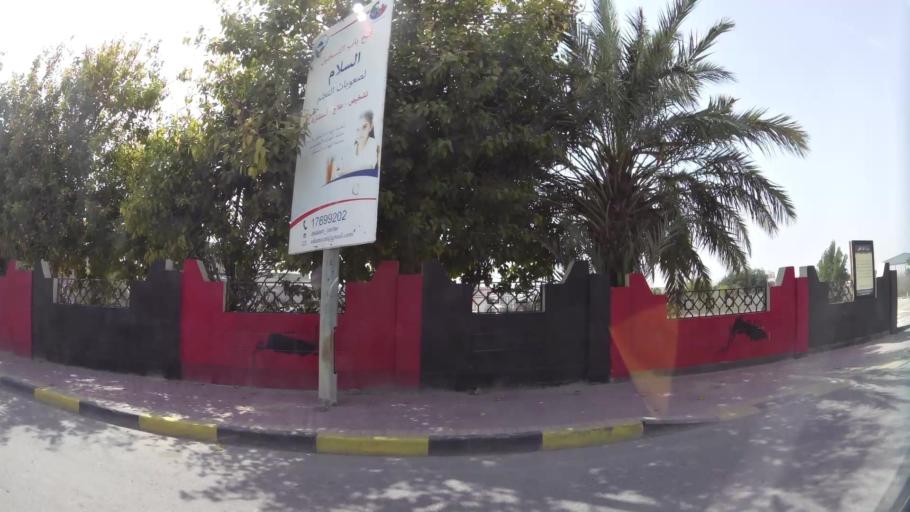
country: BH
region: Manama
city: Jidd Hafs
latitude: 26.2295
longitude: 50.4797
